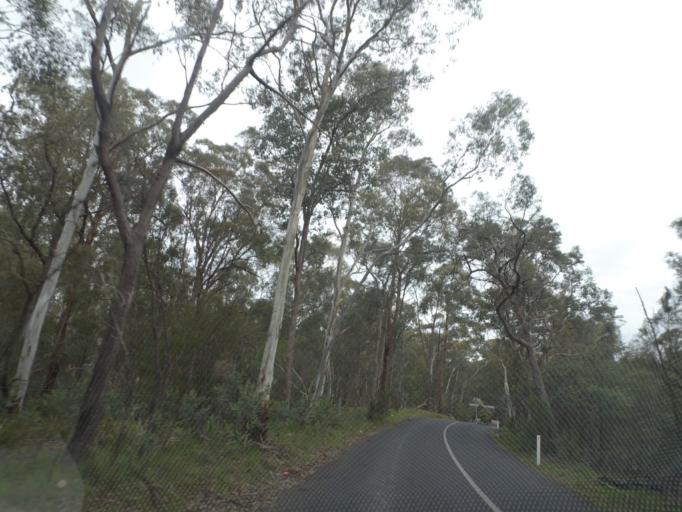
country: AU
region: Victoria
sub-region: Nillumbik
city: Hurstbridge
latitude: -37.6692
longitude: 145.2560
